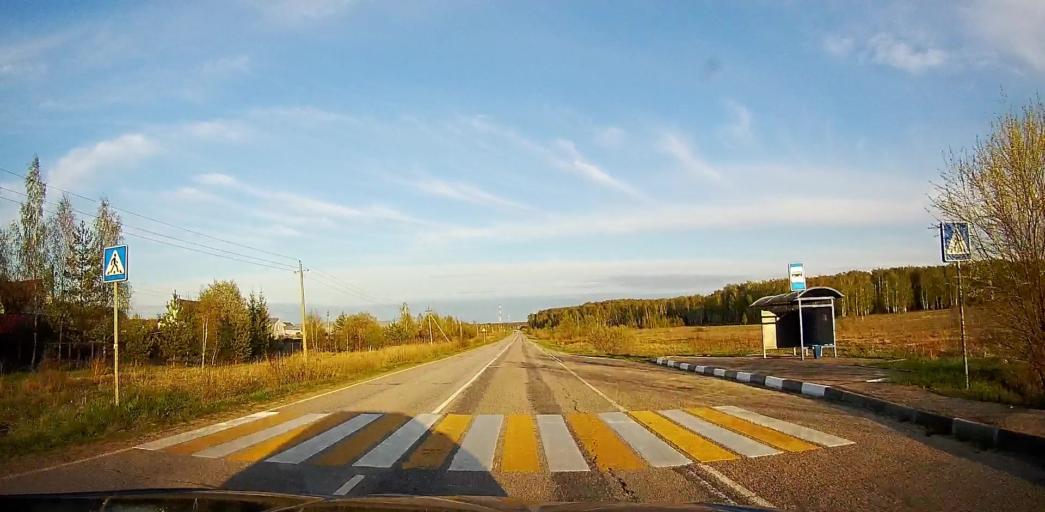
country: RU
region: Moskovskaya
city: Meshcherino
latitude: 55.2406
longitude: 38.3377
